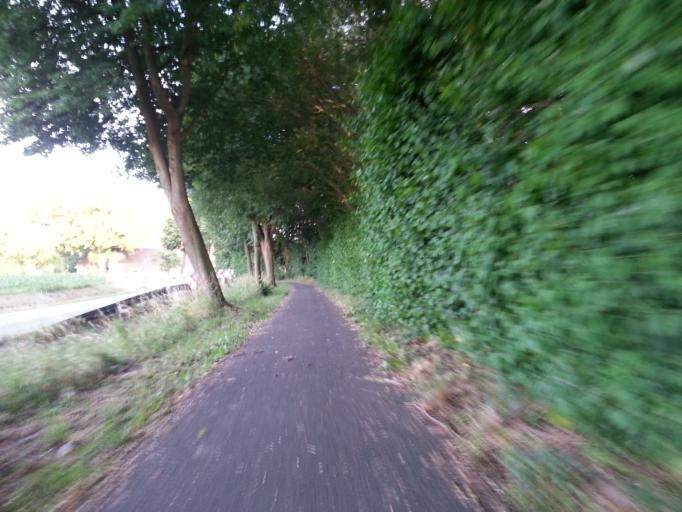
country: DE
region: North Rhine-Westphalia
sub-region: Regierungsbezirk Munster
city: Havixbeck
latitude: 51.9636
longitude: 7.4150
